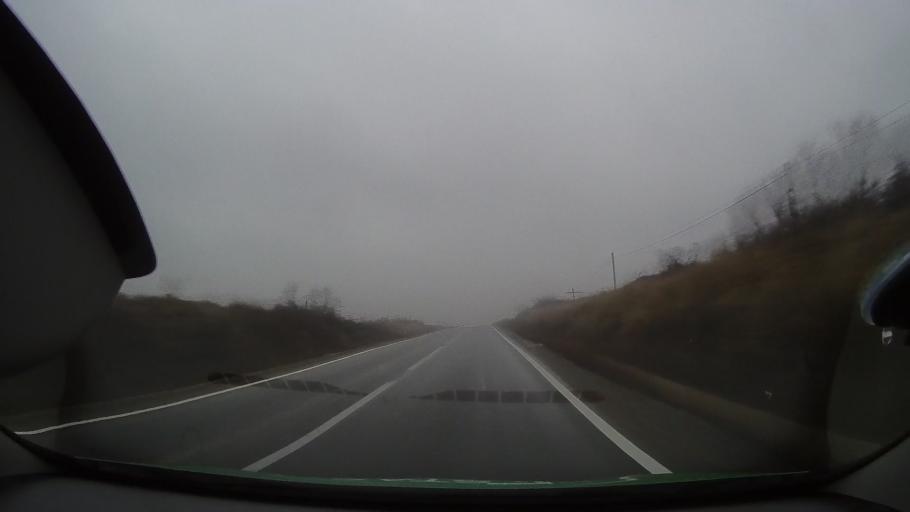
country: RO
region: Bihor
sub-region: Comuna Olcea
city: Olcea
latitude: 46.7119
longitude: 21.9575
